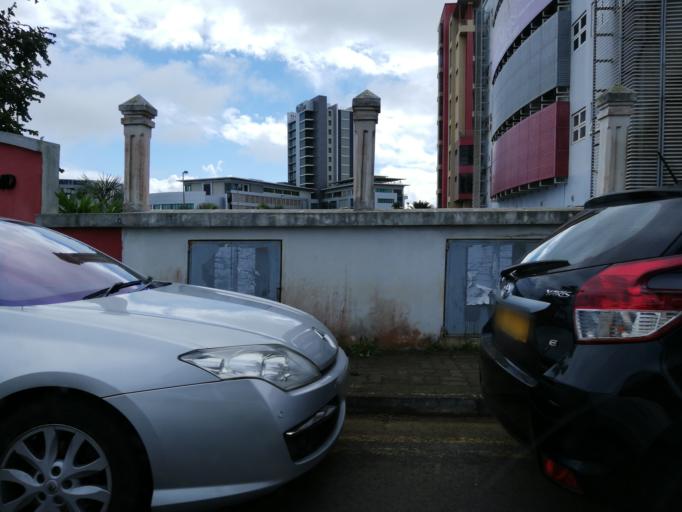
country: MU
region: Plaines Wilhems
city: Ebene
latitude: -20.2456
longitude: 57.4894
